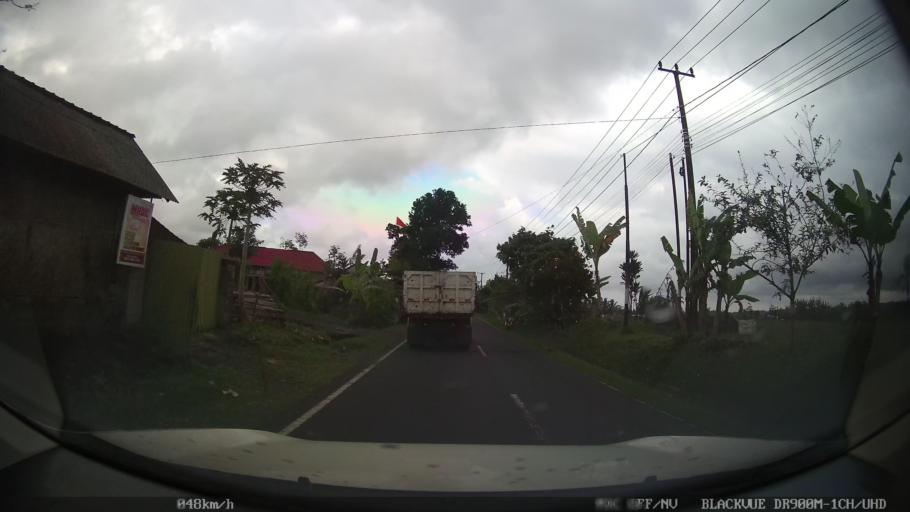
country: ID
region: Bali
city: Empalan
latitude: -8.4037
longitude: 115.1470
